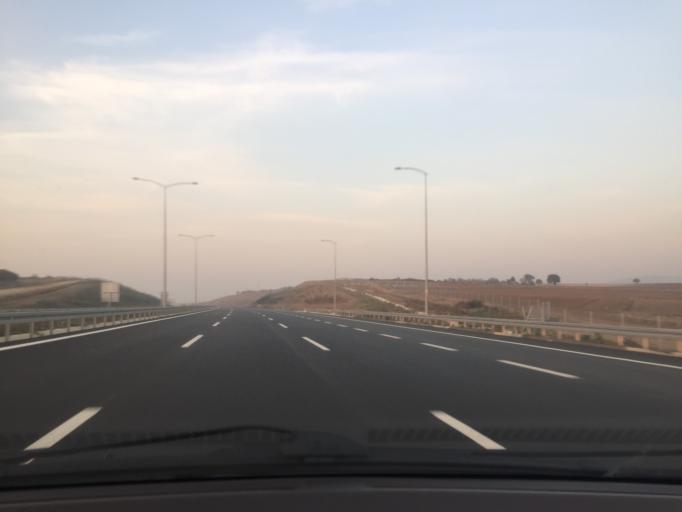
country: TR
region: Bursa
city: Karacabey
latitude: 40.2489
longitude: 28.4434
